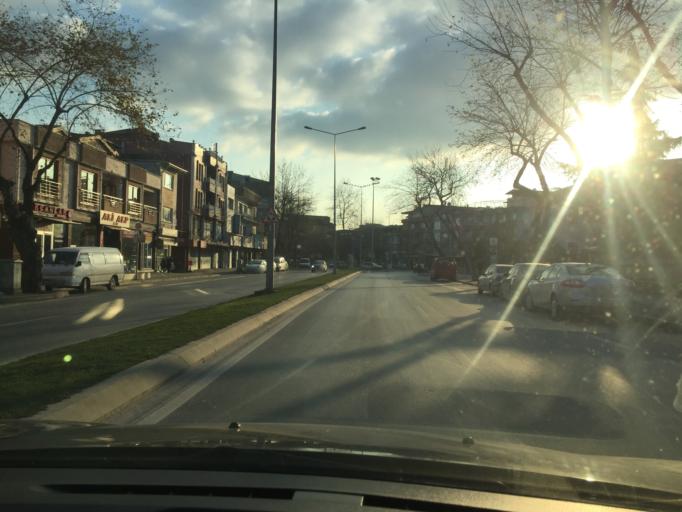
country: TR
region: Sakarya
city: Adapazari
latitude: 40.7857
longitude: 30.4003
